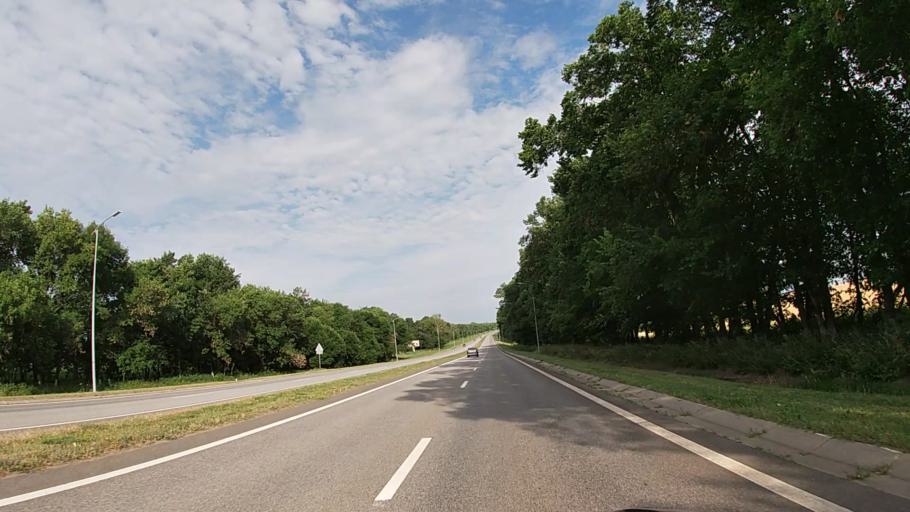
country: RU
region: Belgorod
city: Tomarovka
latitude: 50.6652
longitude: 36.3208
